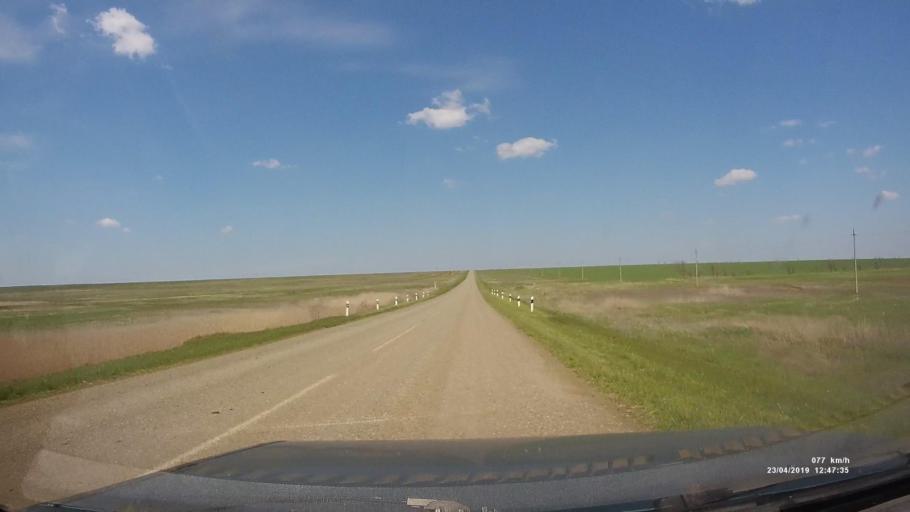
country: RU
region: Kalmykiya
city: Yashalta
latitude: 46.5139
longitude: 42.6386
